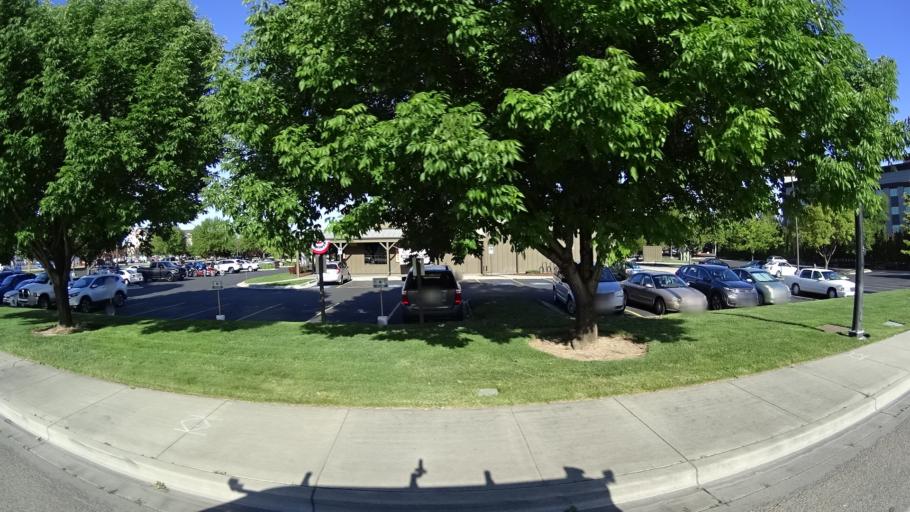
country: US
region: Idaho
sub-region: Ada County
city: Garden City
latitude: 43.5885
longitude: -116.2743
